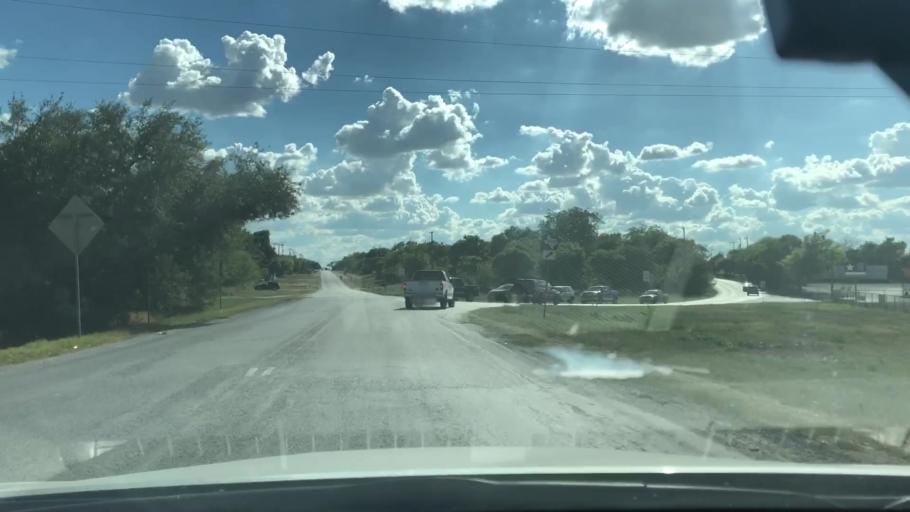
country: US
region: Texas
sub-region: Comal County
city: New Braunfels
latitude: 29.6652
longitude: -98.1727
